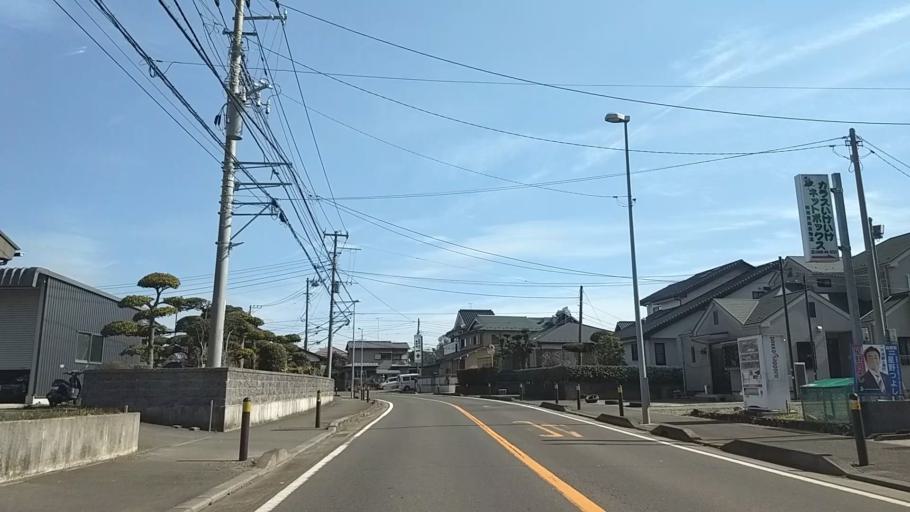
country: JP
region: Kanagawa
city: Chigasaki
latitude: 35.3864
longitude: 139.4111
